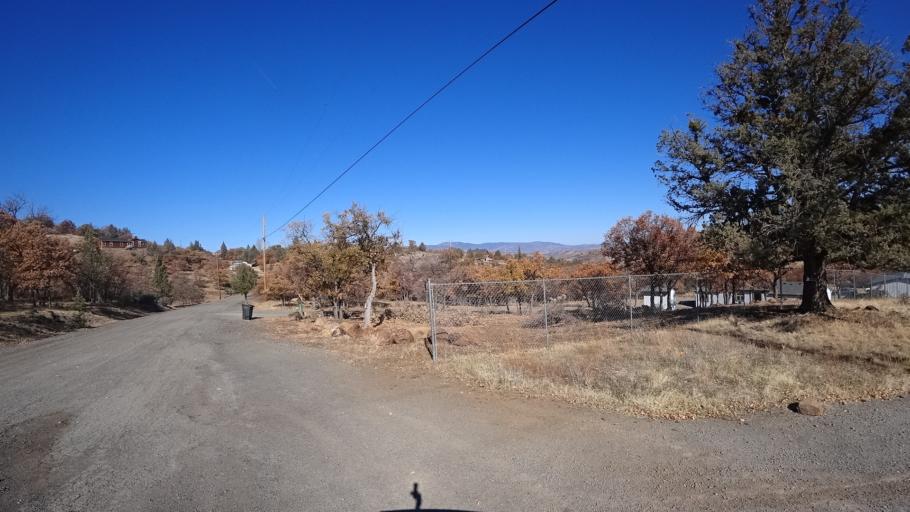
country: US
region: California
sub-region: Siskiyou County
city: Montague
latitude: 41.8734
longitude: -122.4835
